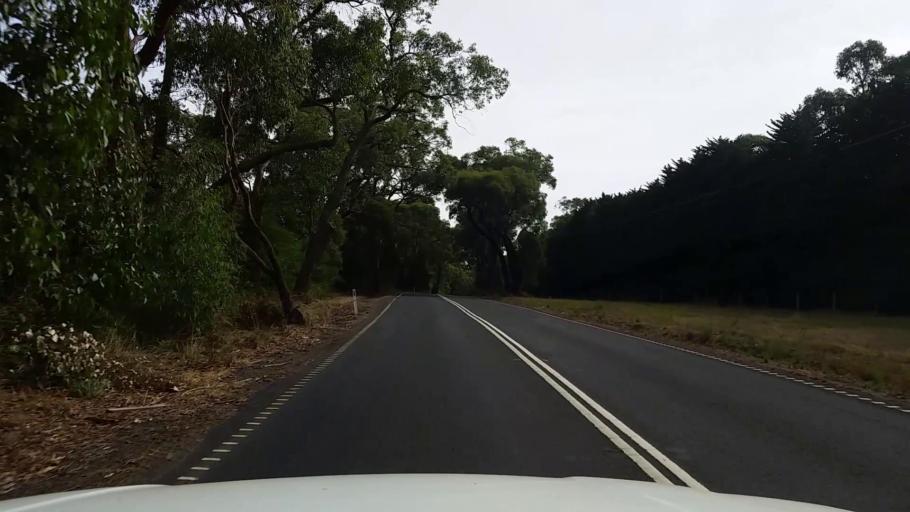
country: AU
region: Victoria
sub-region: Mornington Peninsula
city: Mount Martha
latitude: -38.3040
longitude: 145.0815
